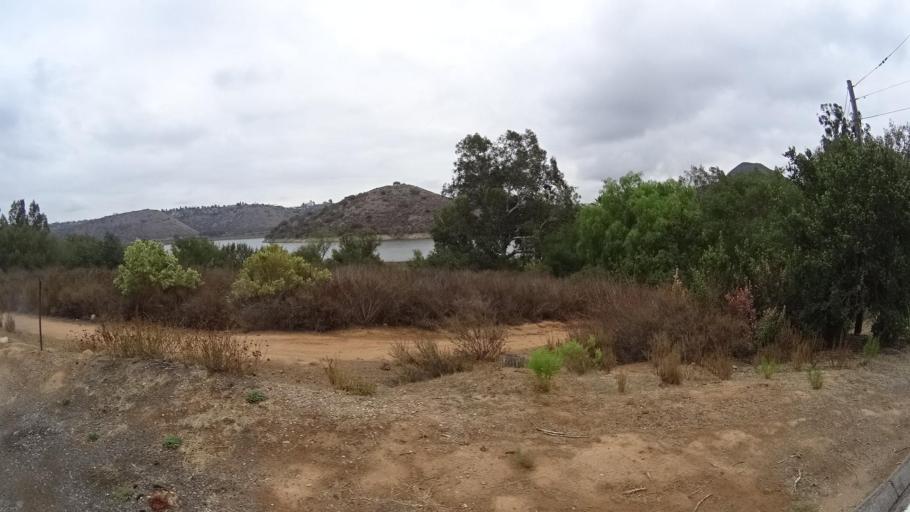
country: US
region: California
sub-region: San Diego County
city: Escondido
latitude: 33.0653
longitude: -117.1203
